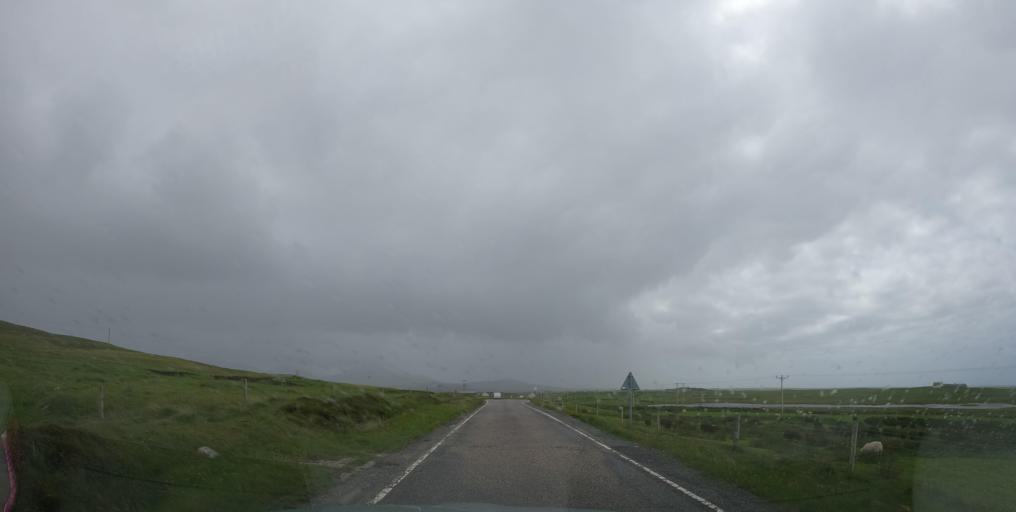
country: GB
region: Scotland
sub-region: Eilean Siar
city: Isle of South Uist
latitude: 57.3421
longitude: -7.3647
